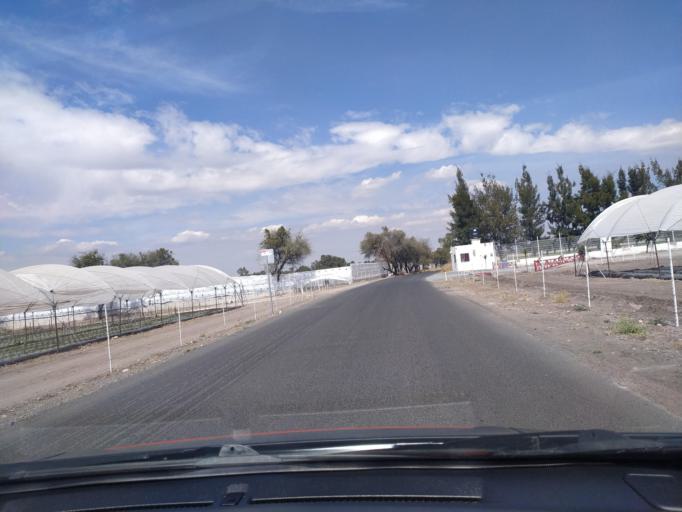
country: MX
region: Guanajuato
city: San Roque
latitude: 20.9628
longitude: -101.8299
